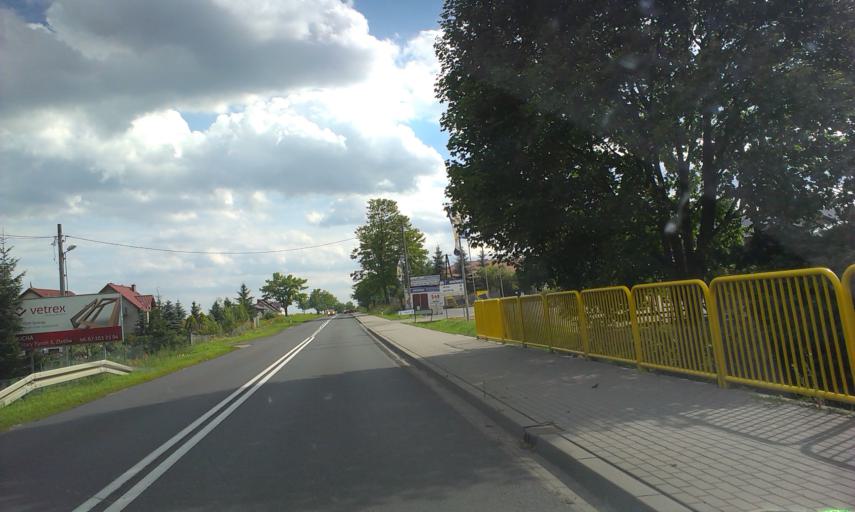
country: PL
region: Greater Poland Voivodeship
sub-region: Powiat zlotowski
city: Zlotow
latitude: 53.3457
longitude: 17.0176
